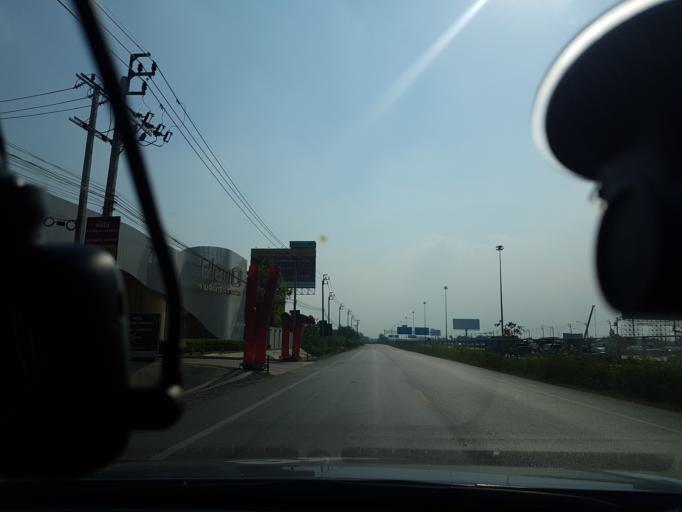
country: TH
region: Pathum Thani
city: Lam Luk Ka
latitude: 13.9149
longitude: 100.7027
